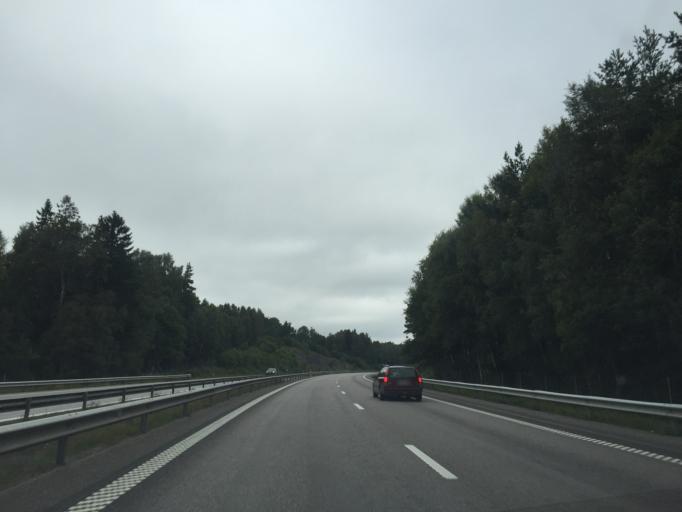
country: SE
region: Halland
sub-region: Kungsbacka Kommun
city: Kungsbacka
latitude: 57.4790
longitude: 12.0441
